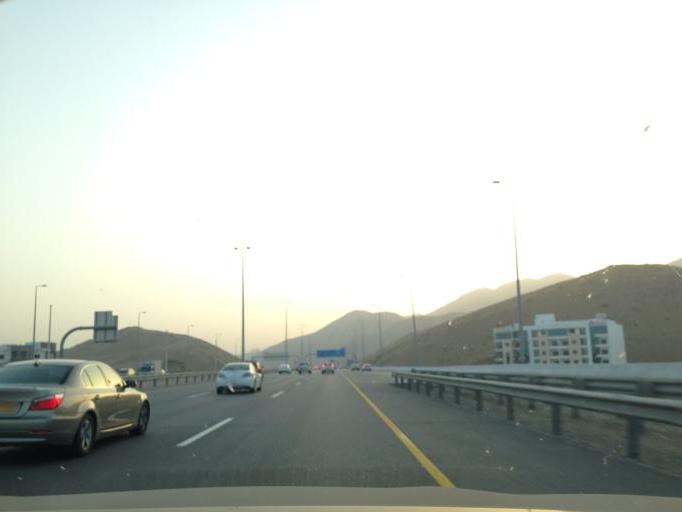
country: OM
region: Muhafazat Masqat
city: Bawshar
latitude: 23.5697
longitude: 58.4129
